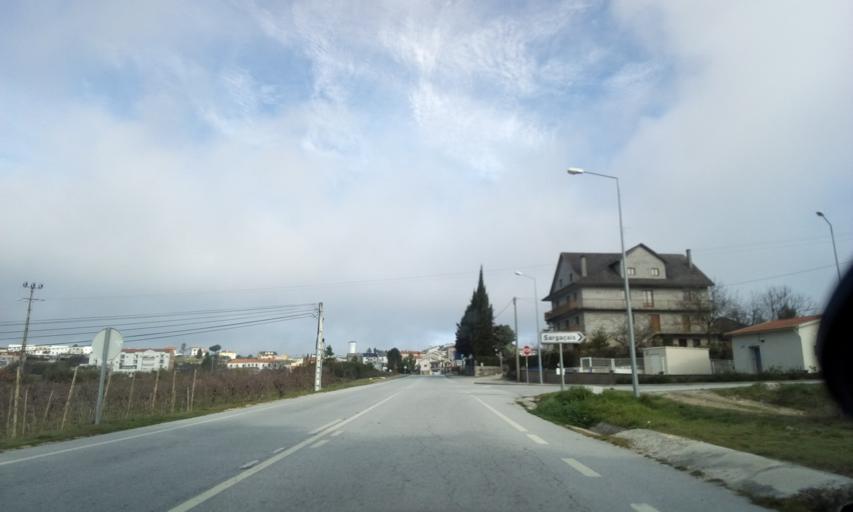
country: PT
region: Guarda
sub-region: Aguiar da Beira
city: Aguiar da Beira
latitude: 40.8141
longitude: -7.5365
